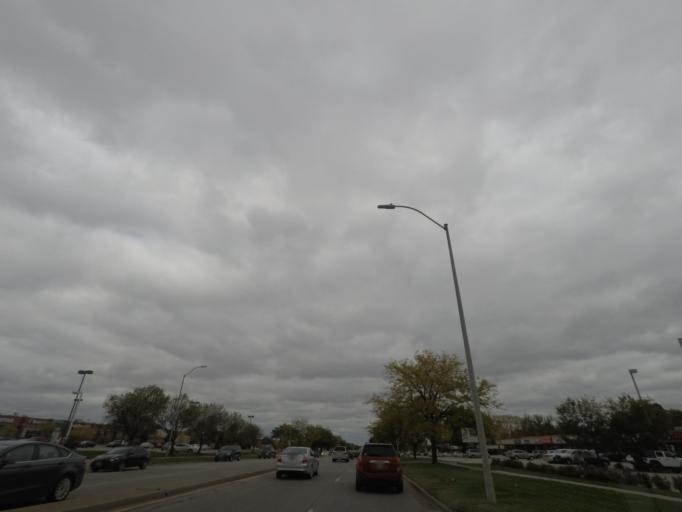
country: US
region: Iowa
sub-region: Polk County
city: Ankeny
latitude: 41.7321
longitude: -93.6003
